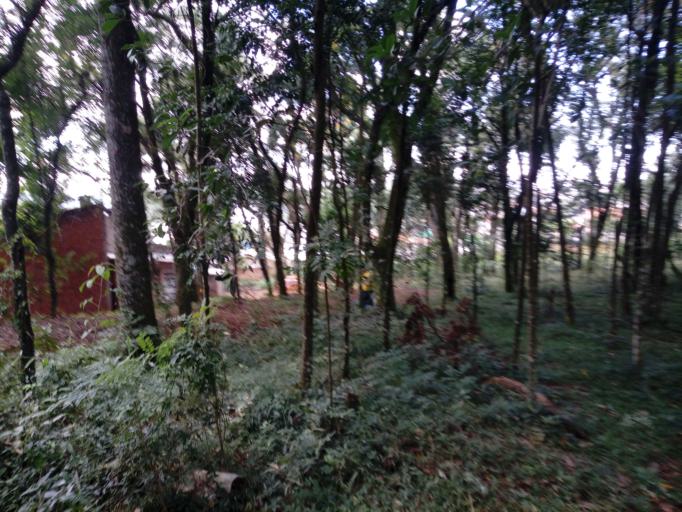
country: BR
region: Santa Catarina
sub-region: Chapeco
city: Chapeco
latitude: -27.1013
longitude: -52.6427
